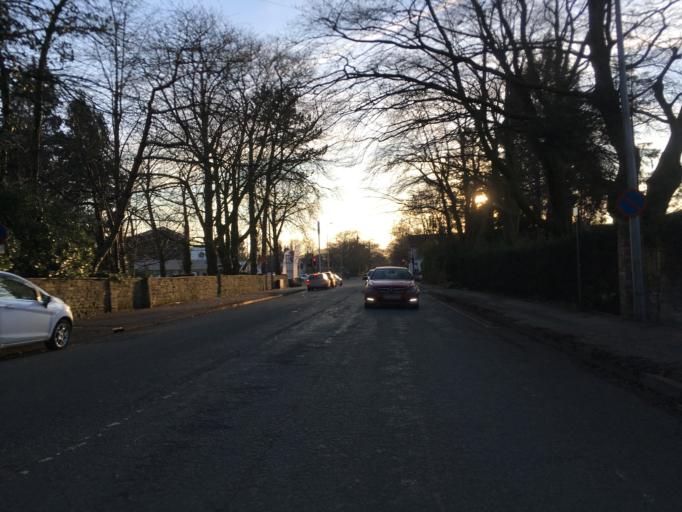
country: GB
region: England
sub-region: Cheshire East
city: Wilmslow
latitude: 53.3397
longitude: -2.2223
